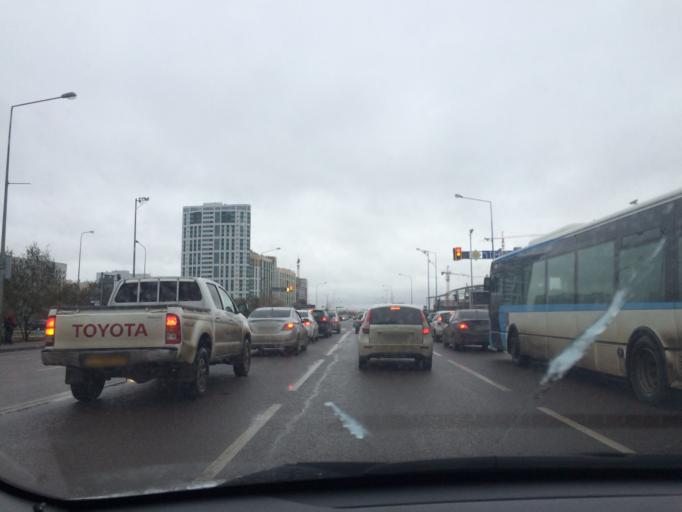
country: KZ
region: Astana Qalasy
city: Astana
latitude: 51.1191
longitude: 71.4119
